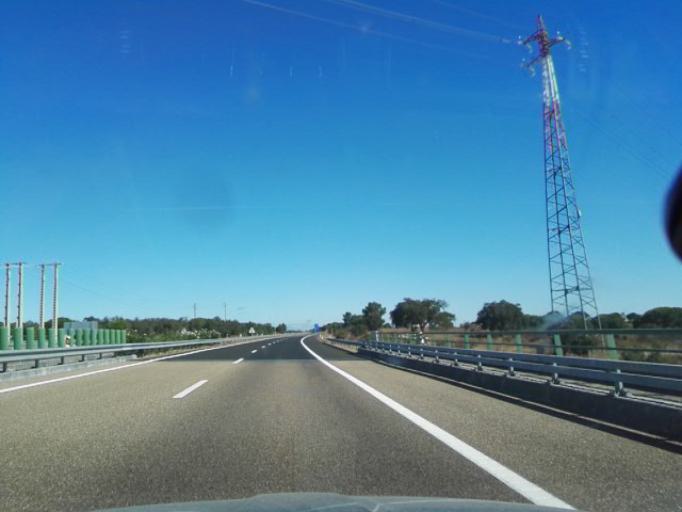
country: PT
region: Santarem
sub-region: Benavente
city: Benavente
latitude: 38.9372
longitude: -8.8191
